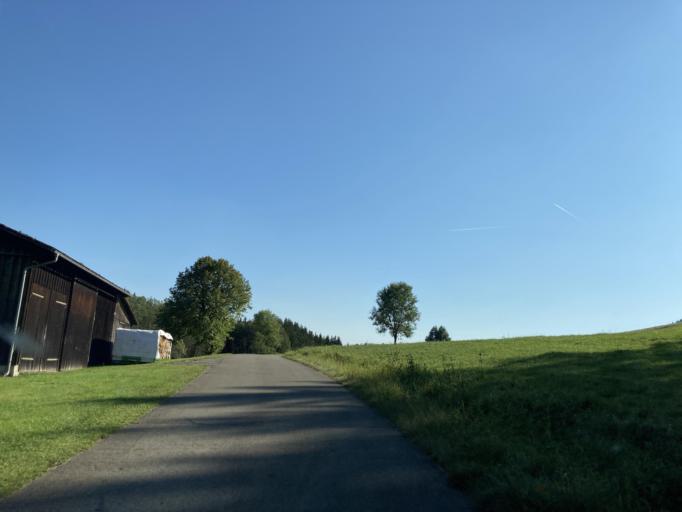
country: DE
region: Baden-Wuerttemberg
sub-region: Freiburg Region
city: Blumberg
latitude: 47.8561
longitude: 8.5036
